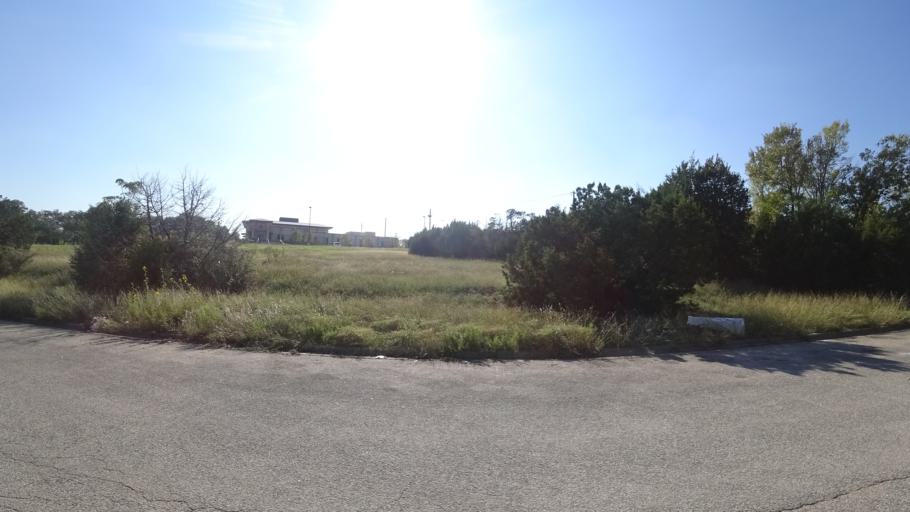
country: US
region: Texas
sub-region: Travis County
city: Austin
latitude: 30.3407
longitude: -97.6800
